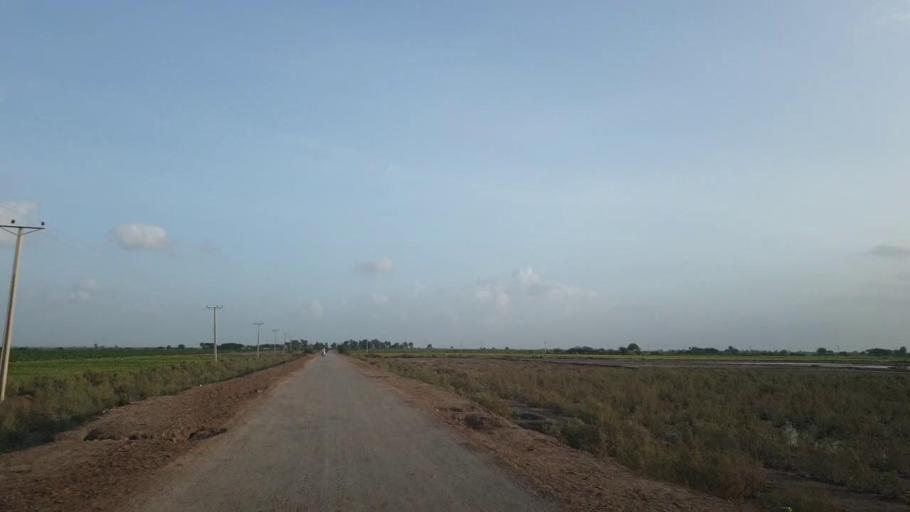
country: PK
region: Sindh
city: Kadhan
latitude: 24.6242
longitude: 69.1158
